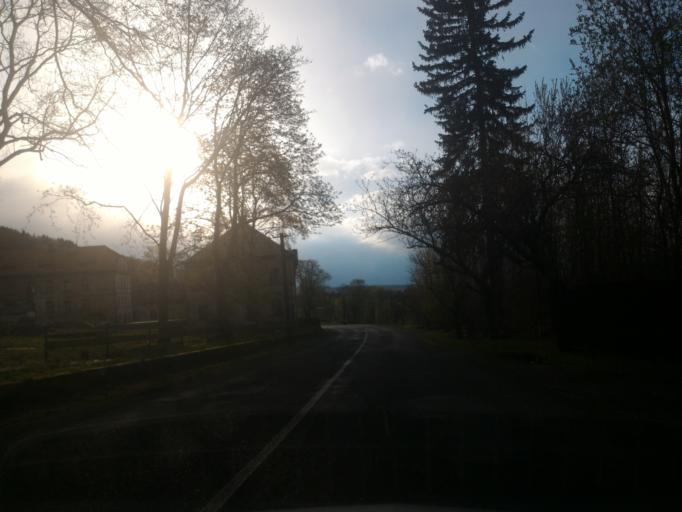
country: CZ
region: Ustecky
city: Dolni Podluzi
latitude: 50.8755
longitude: 14.5705
